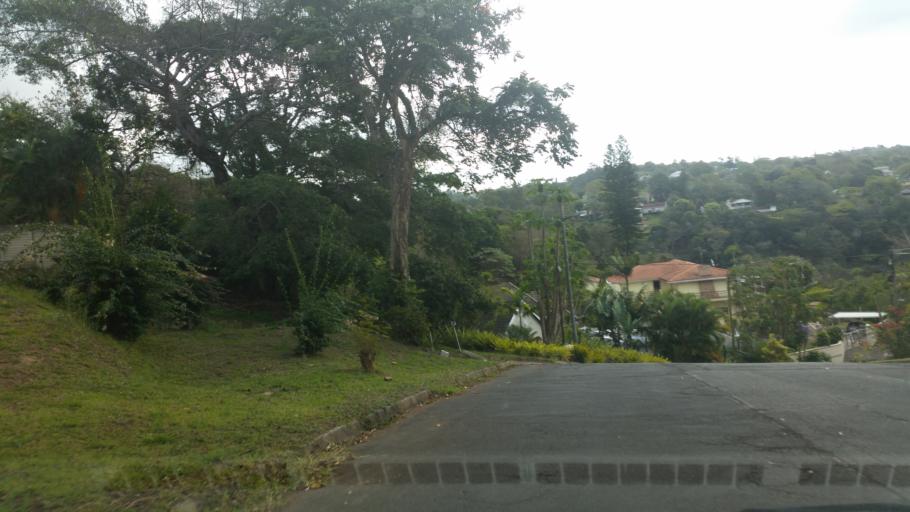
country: ZA
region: KwaZulu-Natal
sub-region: eThekwini Metropolitan Municipality
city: Berea
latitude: -29.8262
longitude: 30.9266
